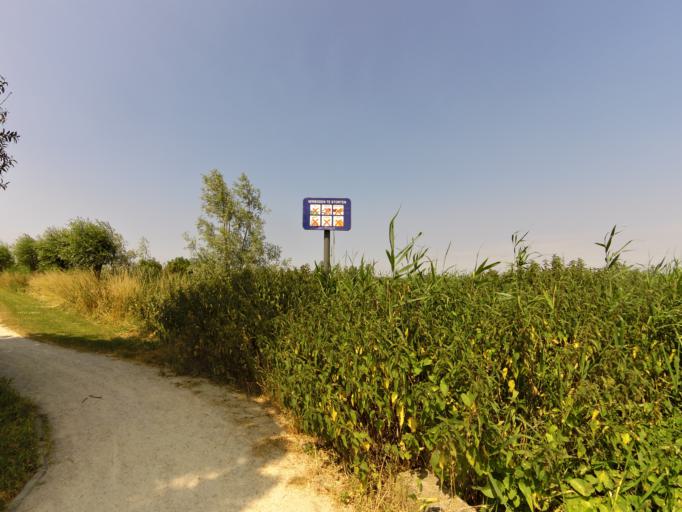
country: BE
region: Flanders
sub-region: Provincie West-Vlaanderen
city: Oudenburg
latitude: 51.1988
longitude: 2.9832
